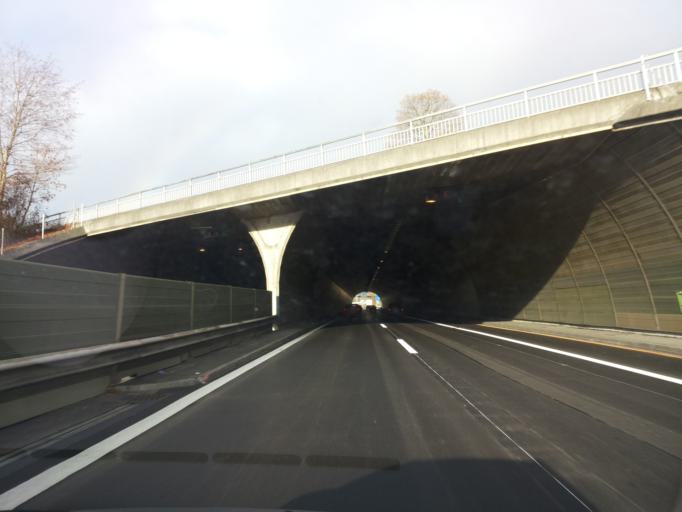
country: CH
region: Lucerne
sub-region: Sursee District
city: Sursee
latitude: 47.1747
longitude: 8.1272
